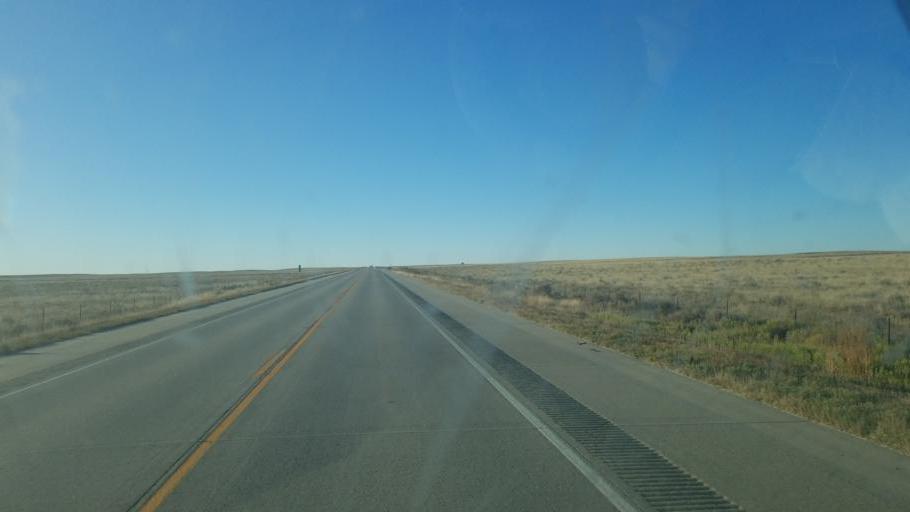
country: US
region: Colorado
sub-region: Kiowa County
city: Eads
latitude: 38.5615
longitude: -102.7862
